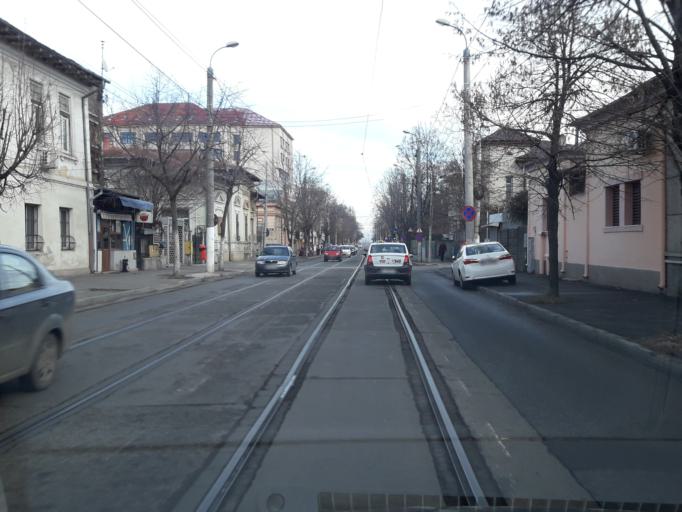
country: RO
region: Galati
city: Galati
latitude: 45.4448
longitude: 28.0502
